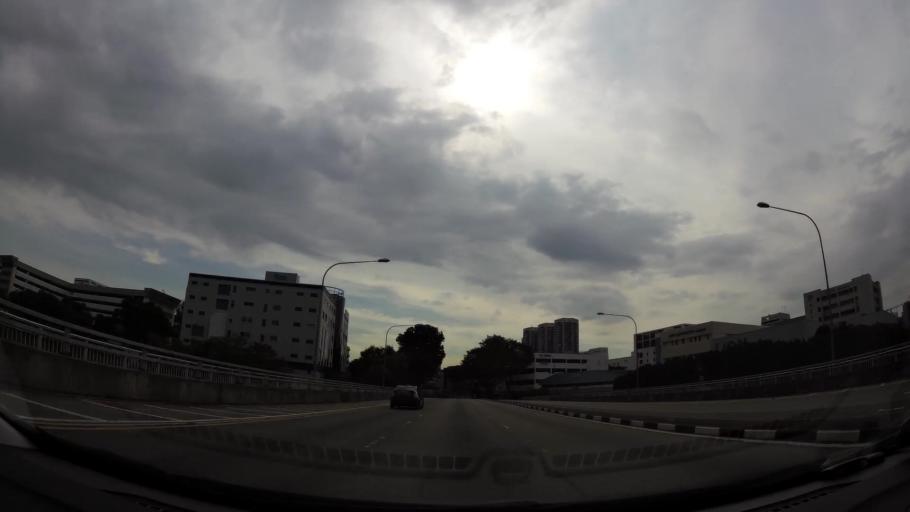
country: SG
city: Singapore
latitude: 1.3187
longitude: 103.8677
